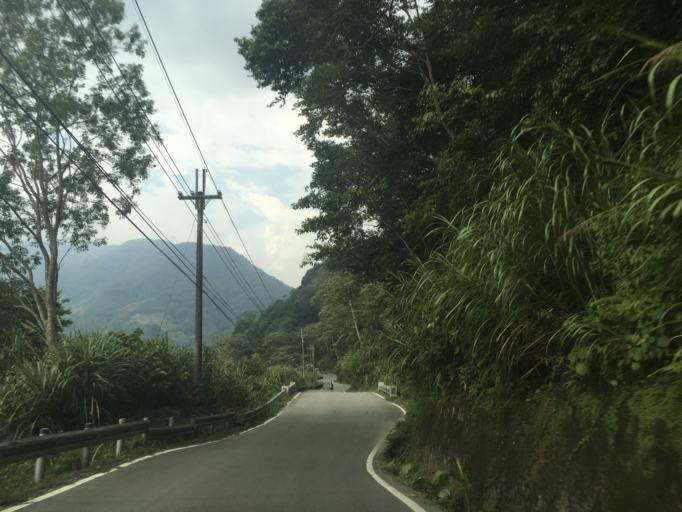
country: TW
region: Taiwan
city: Fengyuan
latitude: 24.3462
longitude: 120.9436
